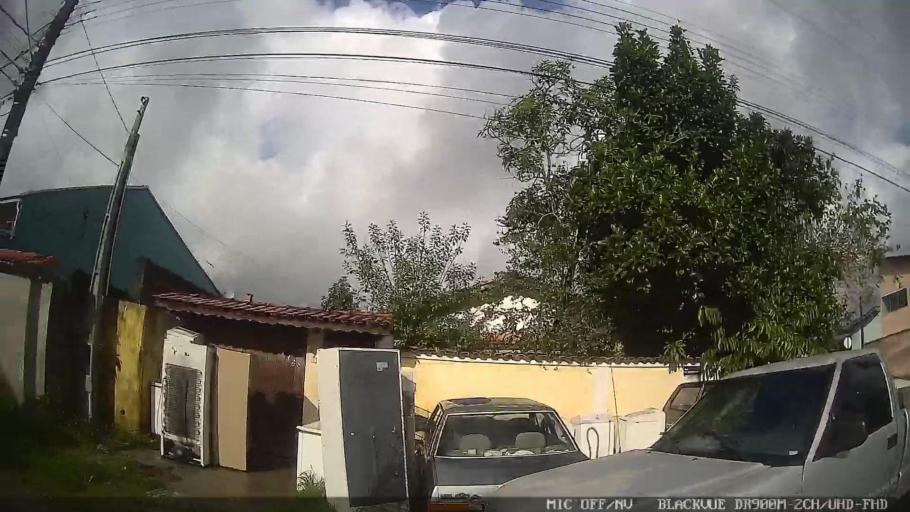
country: BR
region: Sao Paulo
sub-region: Itanhaem
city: Itanhaem
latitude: -24.2199
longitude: -46.8860
